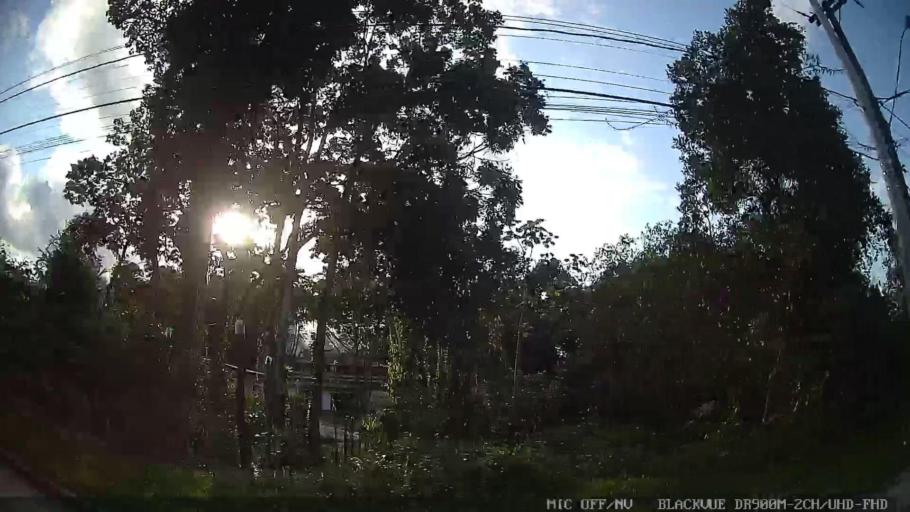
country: BR
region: Sao Paulo
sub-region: Itanhaem
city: Itanhaem
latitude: -24.1506
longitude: -46.8202
